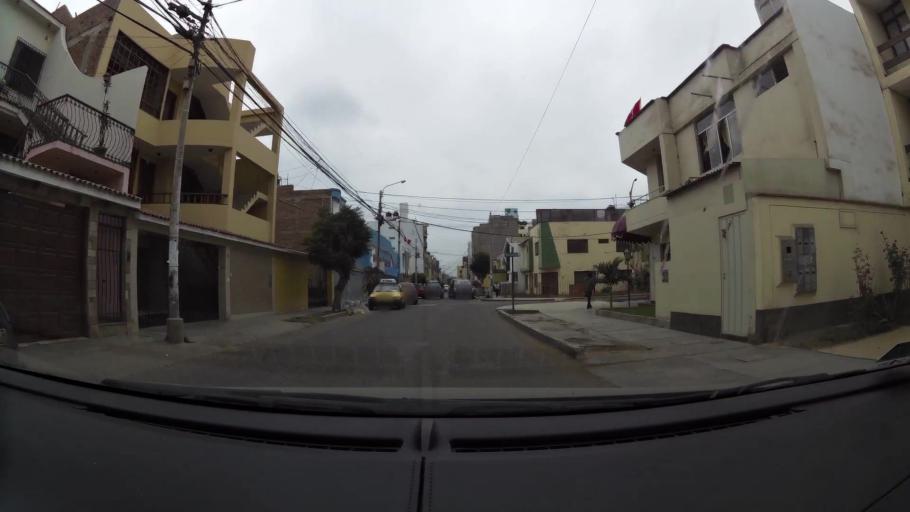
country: PE
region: La Libertad
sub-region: Provincia de Trujillo
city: Buenos Aires
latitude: -8.1314
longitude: -79.0384
